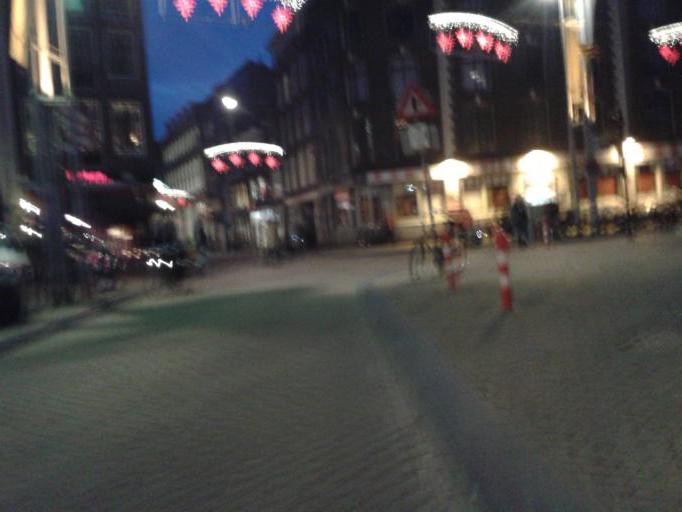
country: NL
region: North Holland
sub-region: Gemeente Amsterdam
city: Amsterdam
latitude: 52.3723
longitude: 4.9006
